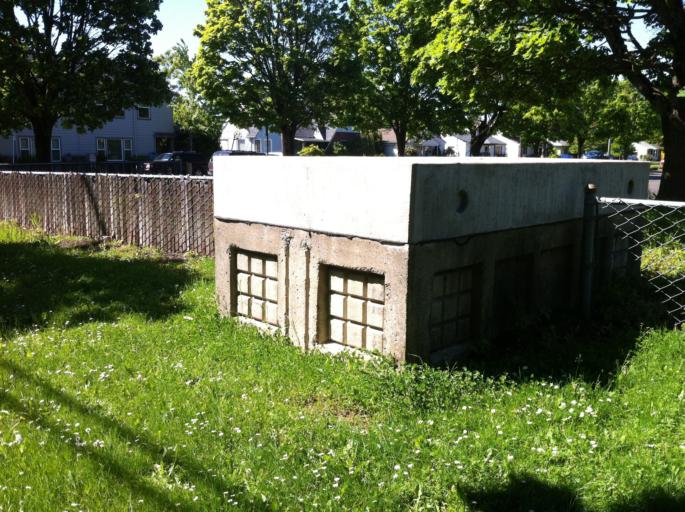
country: US
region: Oregon
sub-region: Multnomah County
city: Lents
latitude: 45.4975
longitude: -122.5919
